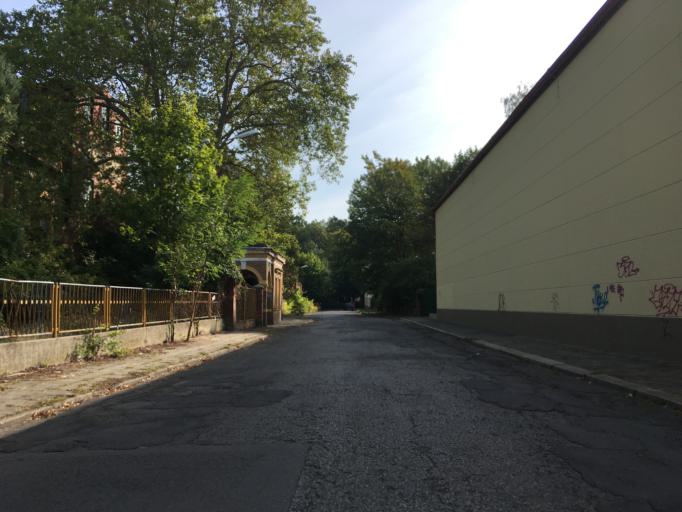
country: DE
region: Brandenburg
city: Forst
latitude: 51.7473
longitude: 14.6532
